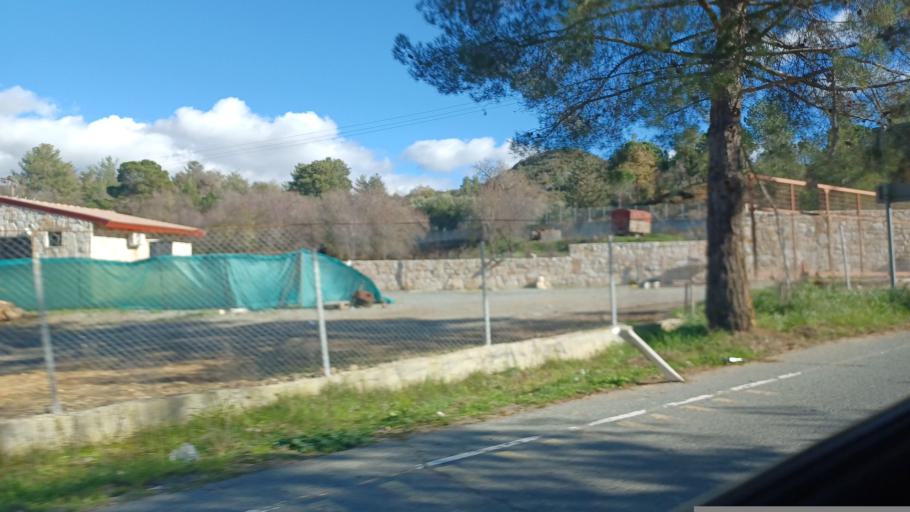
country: CY
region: Limassol
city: Pachna
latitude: 34.8677
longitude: 32.8431
